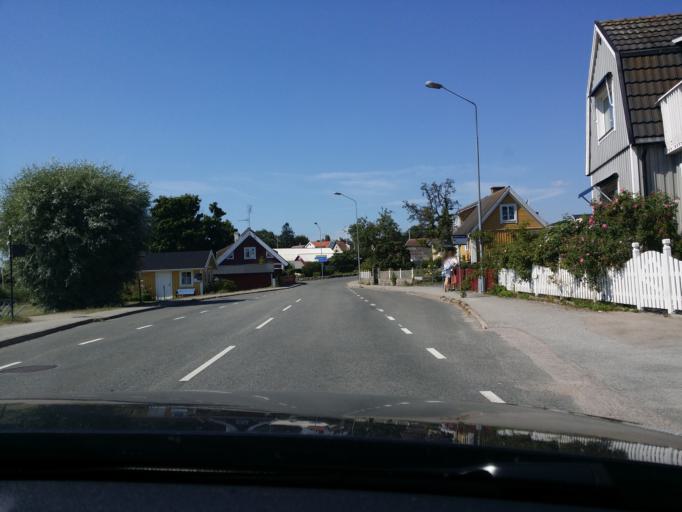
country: SE
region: Blekinge
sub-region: Solvesborgs Kommun
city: Soelvesborg
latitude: 56.0124
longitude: 14.6985
